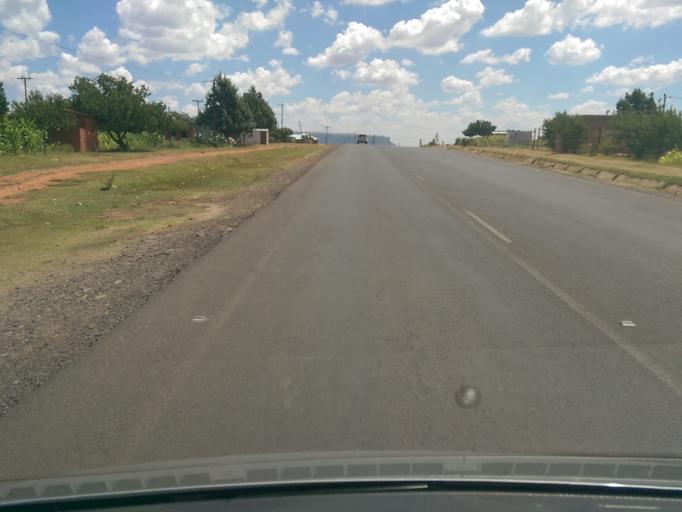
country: LS
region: Maseru
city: Maseru
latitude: -29.4089
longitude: 27.5836
